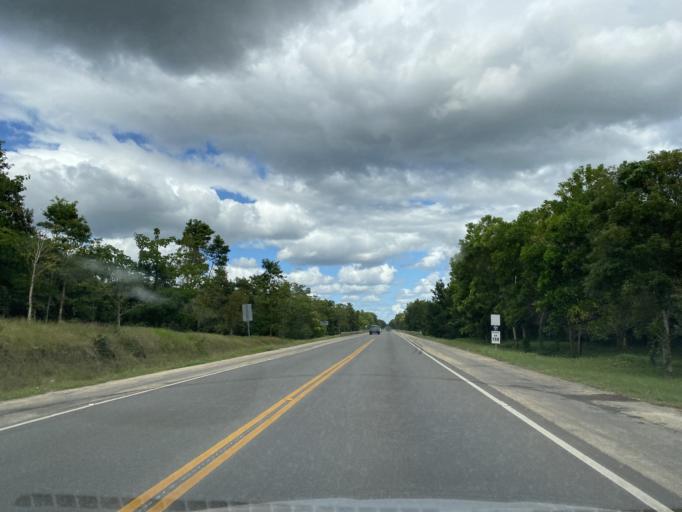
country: DO
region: Santo Domingo
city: Guerra
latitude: 18.6279
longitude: -69.7612
